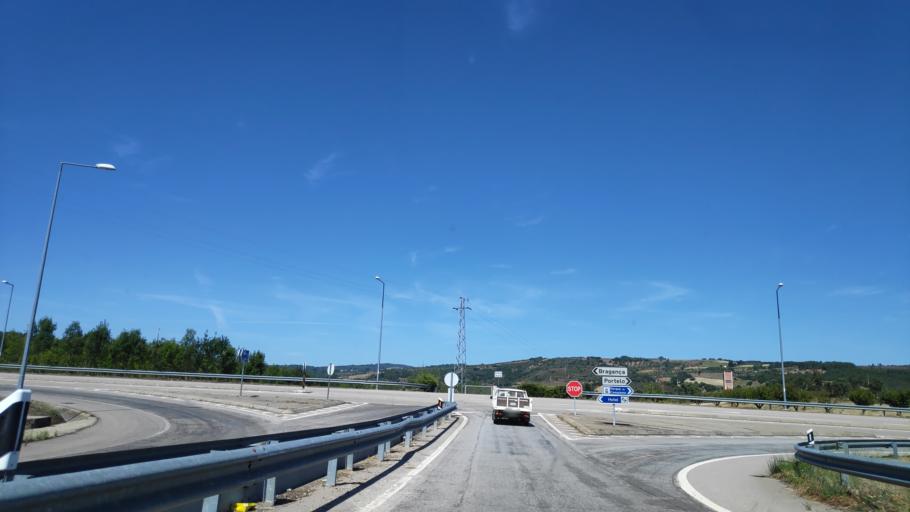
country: PT
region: Braganca
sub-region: Braganca Municipality
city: Braganca
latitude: 41.8221
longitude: -6.7534
